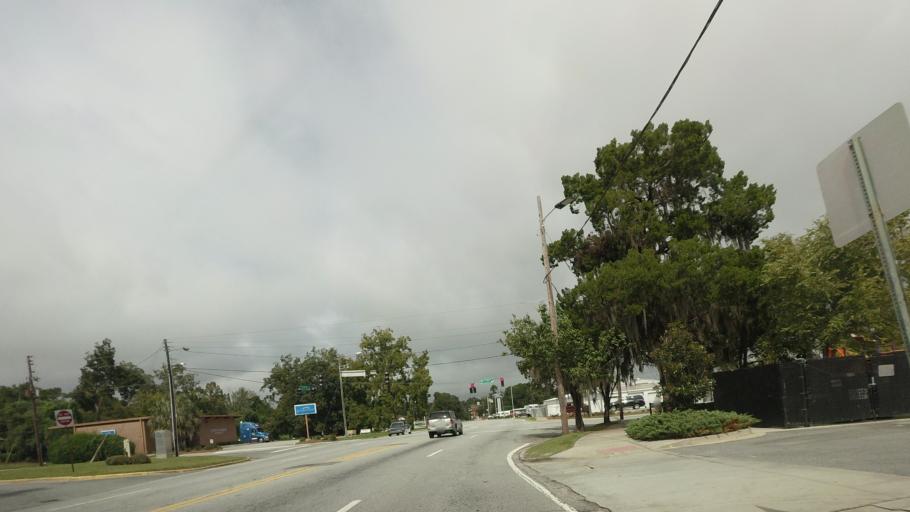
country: US
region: Georgia
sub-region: Lowndes County
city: Valdosta
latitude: 30.8312
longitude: -83.2824
